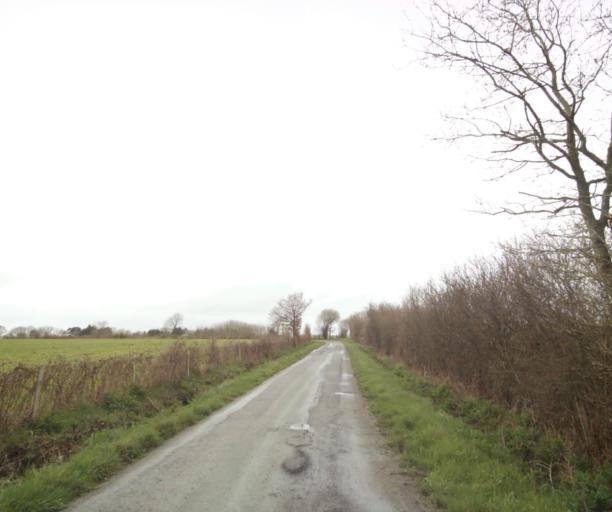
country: FR
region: Pays de la Loire
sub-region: Departement de la Loire-Atlantique
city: Bouvron
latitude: 47.4378
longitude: -1.8766
